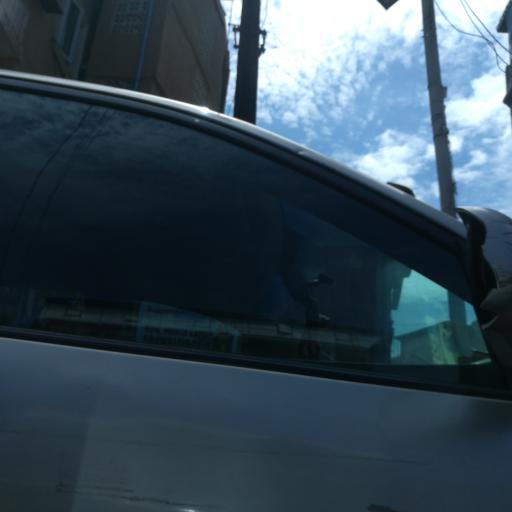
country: NG
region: Lagos
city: Lagos
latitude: 6.4640
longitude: 3.3897
